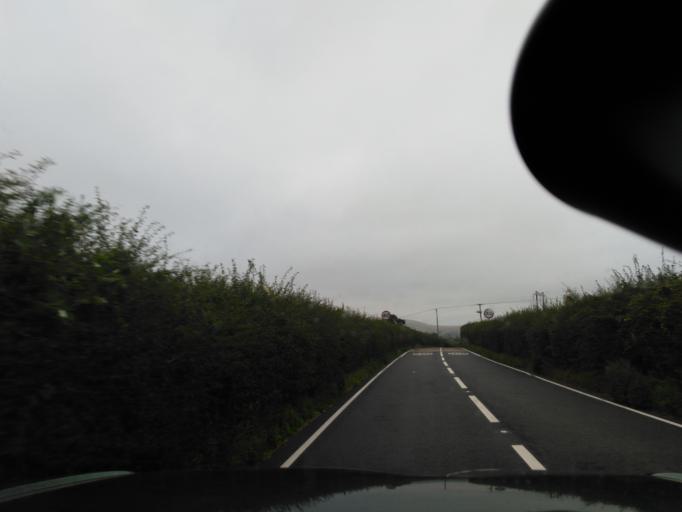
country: GB
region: England
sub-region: Dorset
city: Shaftesbury
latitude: 50.9446
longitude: -2.1949
